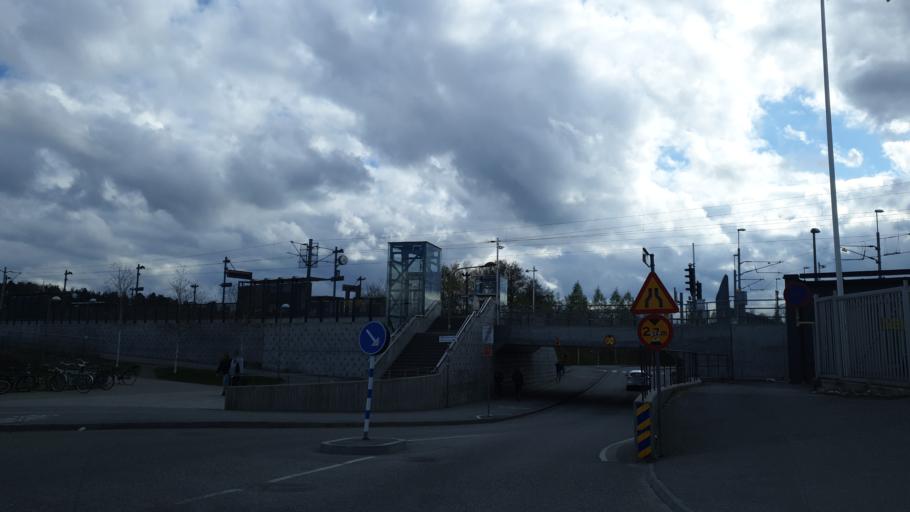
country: SE
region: Stockholm
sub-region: Sundbybergs Kommun
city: Sundbyberg
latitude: 59.3434
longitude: 17.9696
